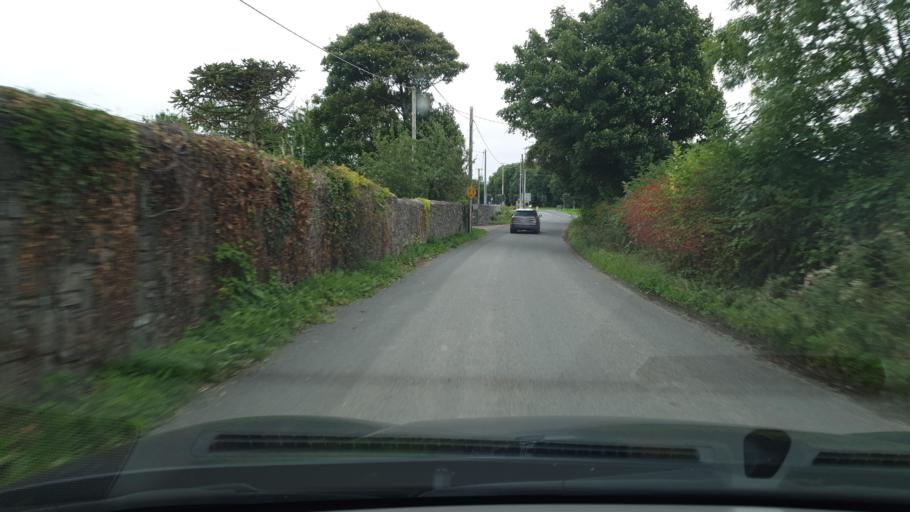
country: IE
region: Leinster
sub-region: An Mhi
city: Ratoath
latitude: 53.5513
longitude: -6.4498
